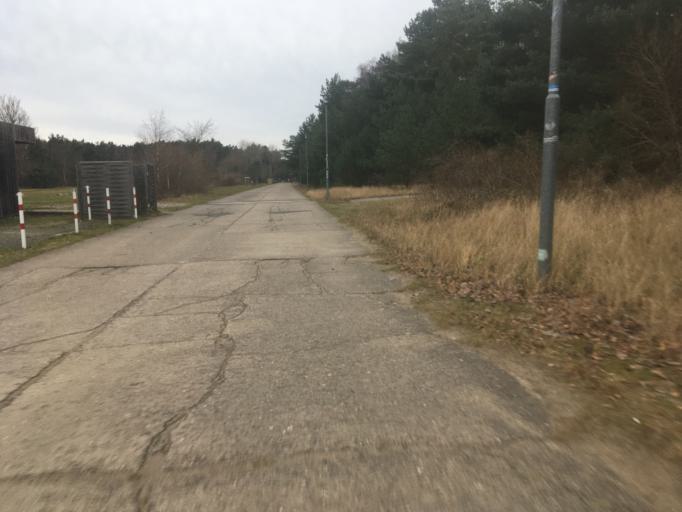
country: DE
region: Mecklenburg-Vorpommern
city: Ostseebad Binz
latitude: 54.4541
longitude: 13.5683
